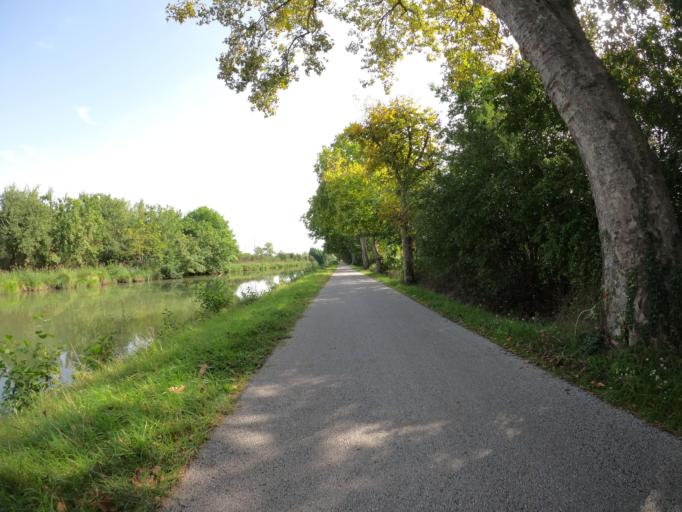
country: FR
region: Midi-Pyrenees
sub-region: Departement de la Haute-Garonne
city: Saint-Jory
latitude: 43.7292
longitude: 1.3768
